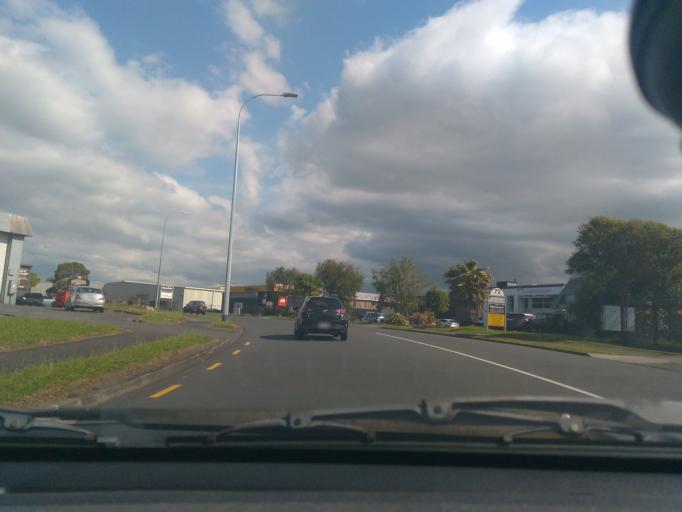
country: NZ
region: Auckland
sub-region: Auckland
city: Manukau City
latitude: -36.9452
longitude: 174.8814
